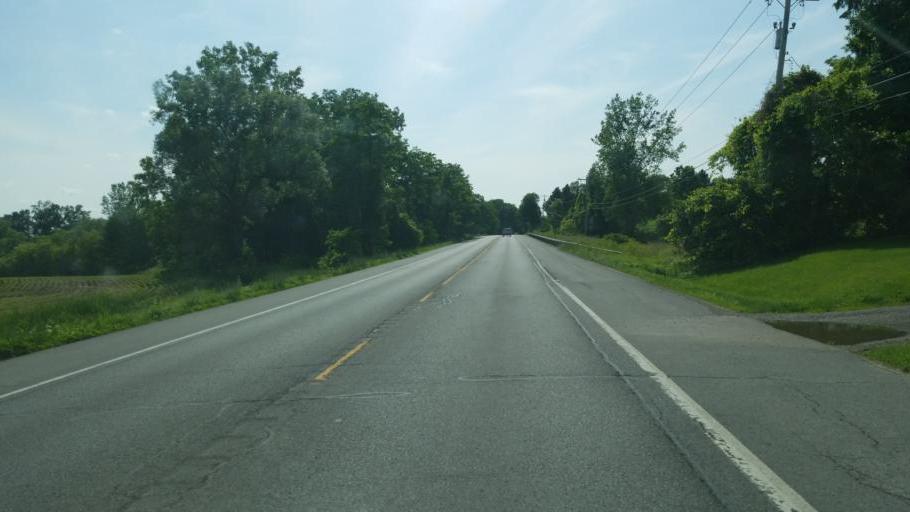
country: US
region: New York
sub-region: Ontario County
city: Holcomb
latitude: 42.9035
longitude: -77.5104
